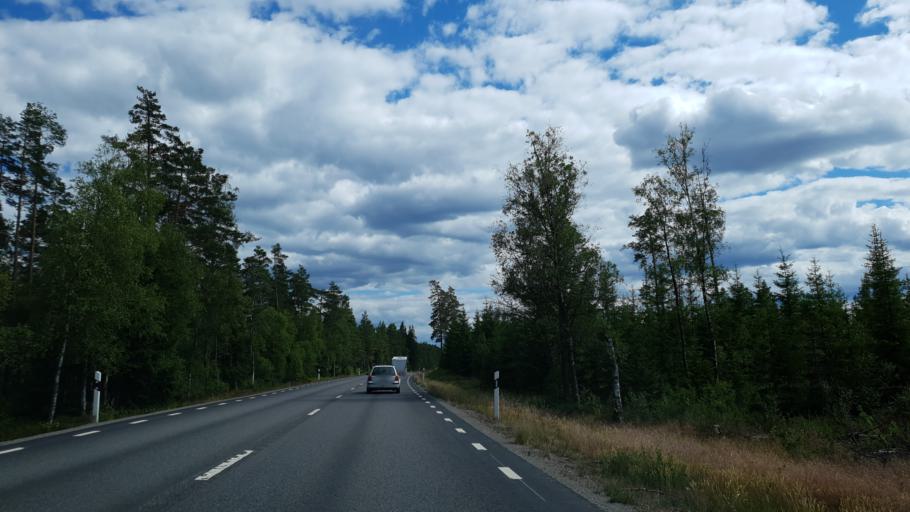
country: SE
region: Kronoberg
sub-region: Lessebo Kommun
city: Lessebo
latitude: 56.8273
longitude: 15.4015
